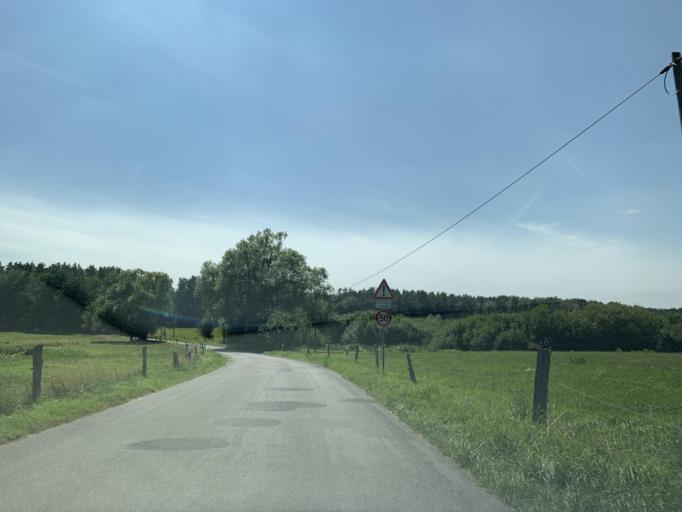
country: DE
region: Mecklenburg-Vorpommern
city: Carpin
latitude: 53.3229
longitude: 13.2447
